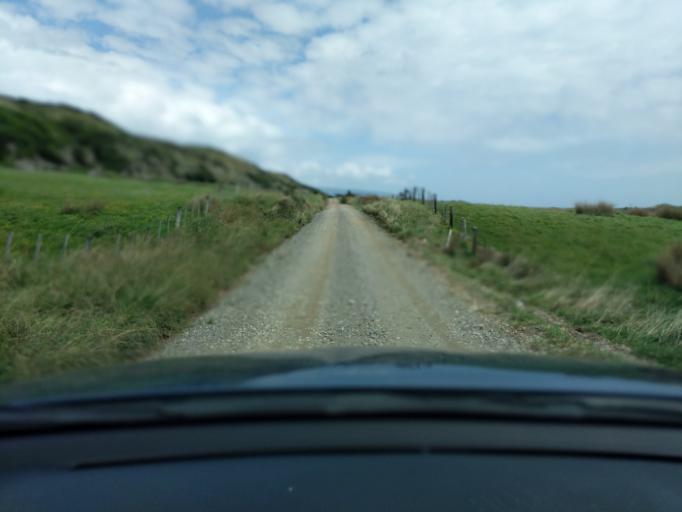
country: NZ
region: Tasman
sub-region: Tasman District
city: Takaka
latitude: -40.6644
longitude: 172.4090
